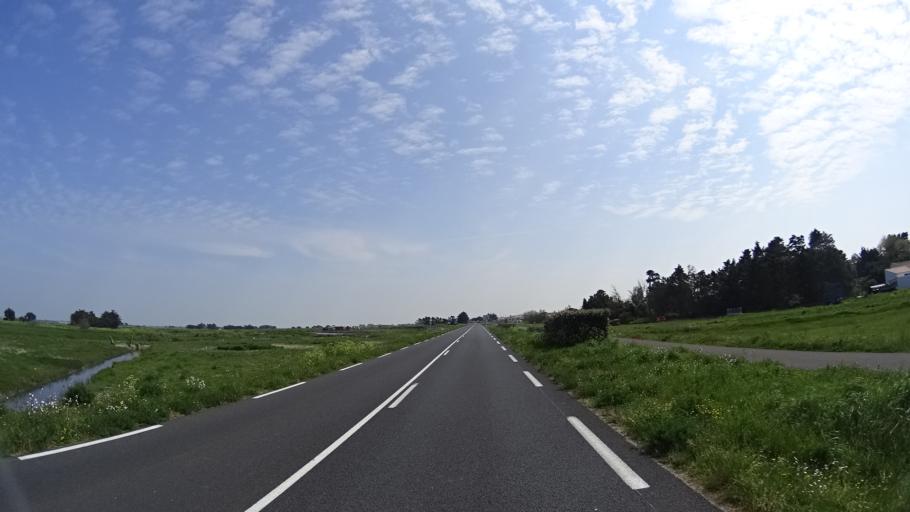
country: FR
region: Pays de la Loire
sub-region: Departement de la Vendee
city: La Gueriniere
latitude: 46.9877
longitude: -2.2823
